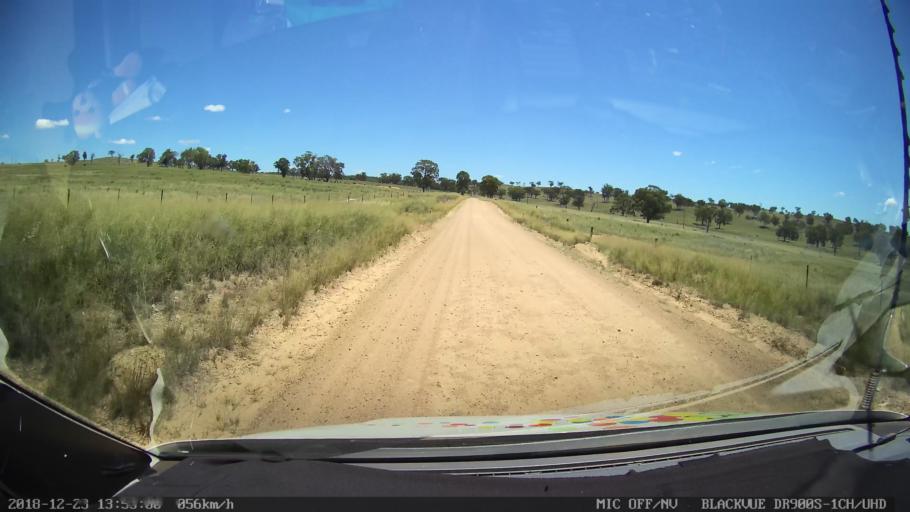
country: AU
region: New South Wales
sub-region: Tamworth Municipality
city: Manilla
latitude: -30.5508
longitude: 151.0987
